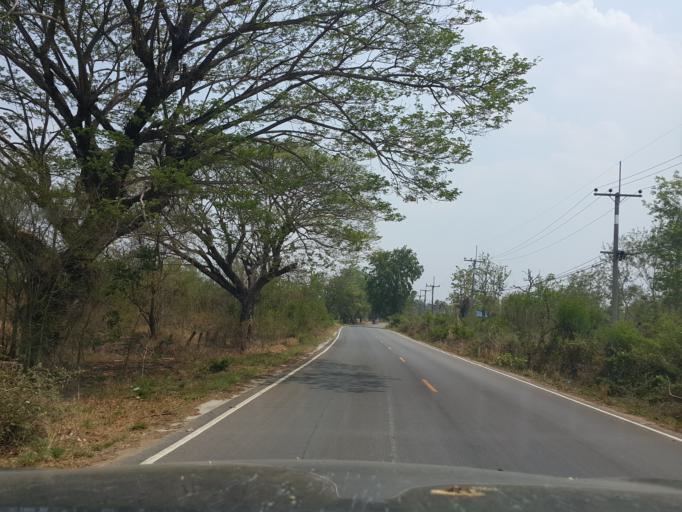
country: TH
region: Lampang
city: Mae Phrik
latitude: 17.4940
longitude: 99.1253
